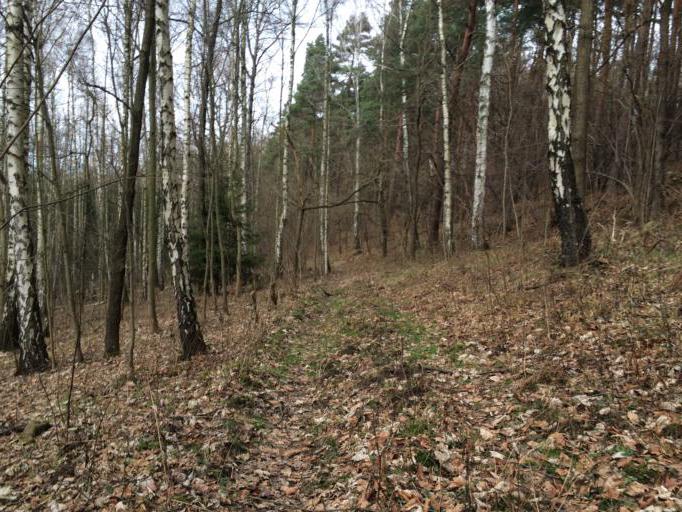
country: PL
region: Lower Silesian Voivodeship
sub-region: Powiat lwowecki
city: Lwowek Slaski
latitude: 51.1071
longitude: 15.6236
